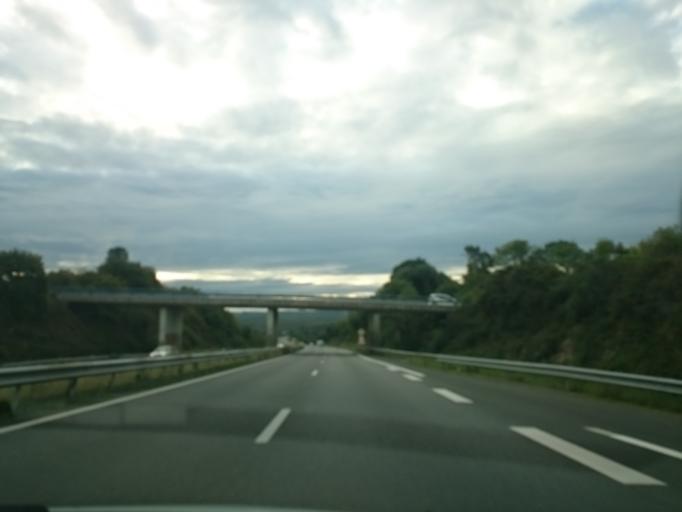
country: FR
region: Brittany
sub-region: Departement du Finistere
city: Le Faou
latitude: 48.3053
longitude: -4.1897
